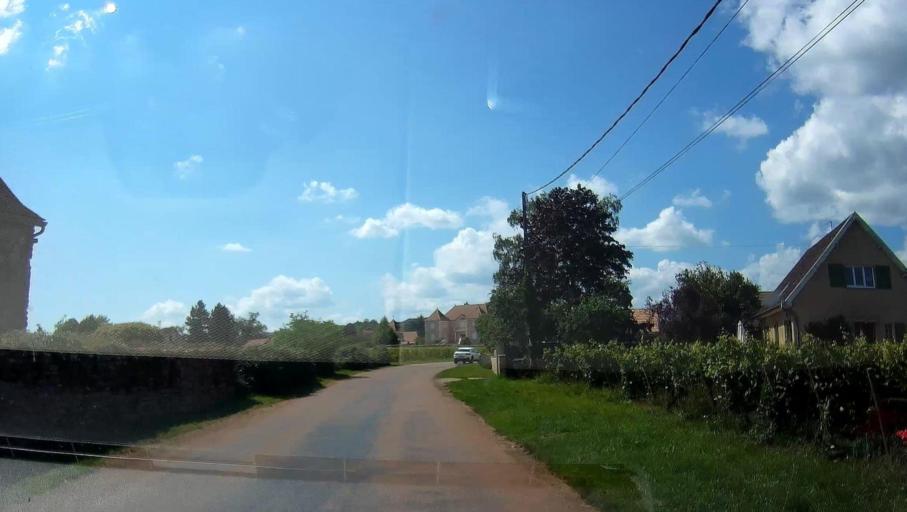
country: FR
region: Bourgogne
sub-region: Departement de Saone-et-Loire
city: Saint-Leger-sur-Dheune
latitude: 46.8943
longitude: 4.6678
